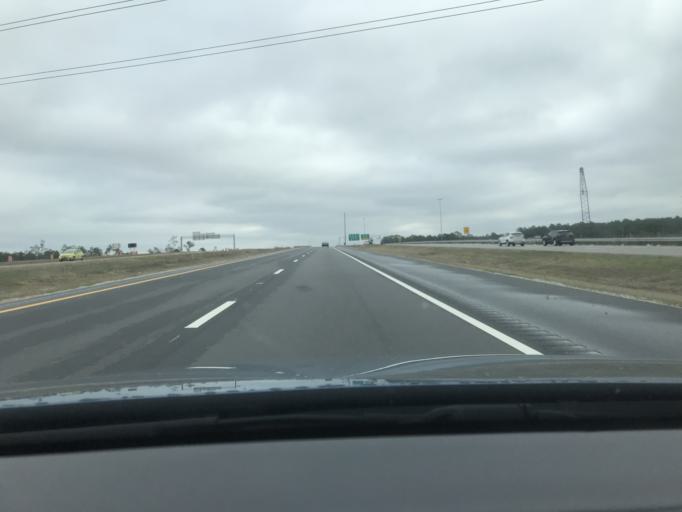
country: US
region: North Carolina
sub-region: Cumberland County
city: Fort Bragg
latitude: 35.1132
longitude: -78.9644
